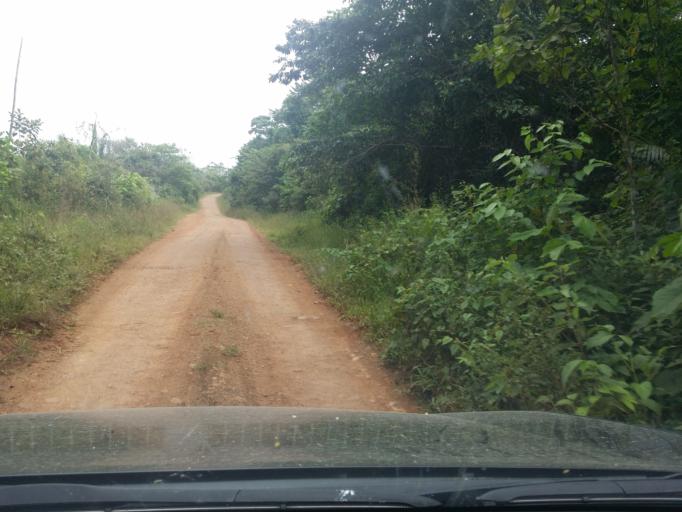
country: CR
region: Alajuela
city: Los Chiles
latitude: 11.0710
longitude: -84.5002
